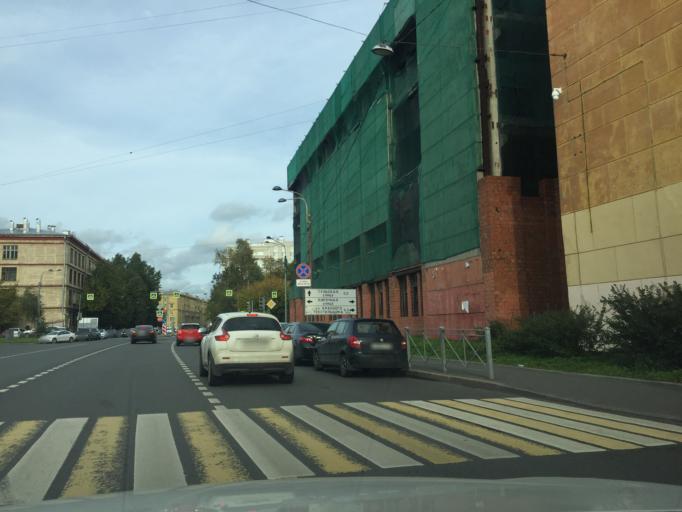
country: RU
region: St.-Petersburg
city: Centralniy
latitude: 59.9389
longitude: 30.3881
